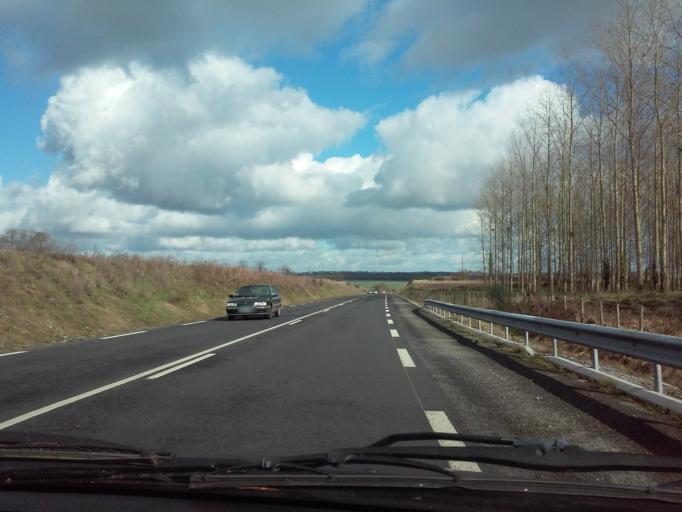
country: FR
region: Brittany
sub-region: Departement d'Ille-et-Vilaine
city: Poce-les-Bois
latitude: 48.0867
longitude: -1.2418
